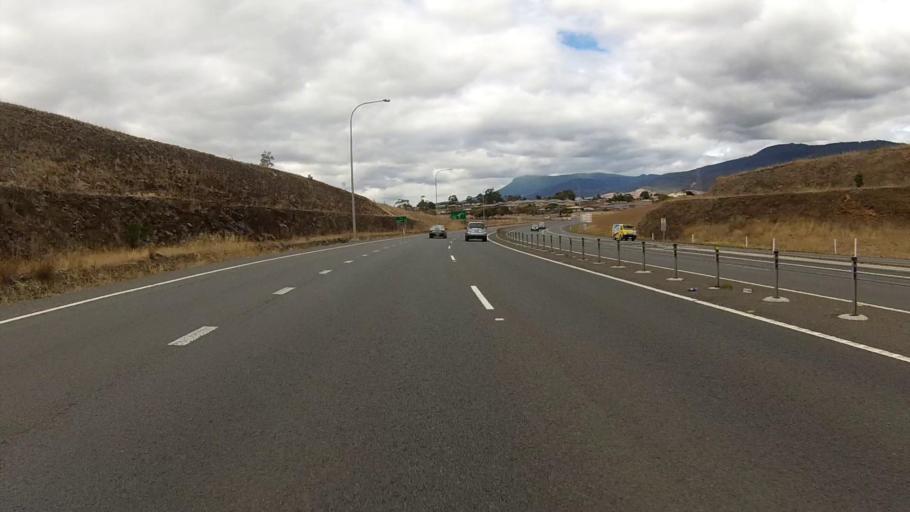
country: AU
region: Tasmania
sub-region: Brighton
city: Bridgewater
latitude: -42.7295
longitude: 147.2377
